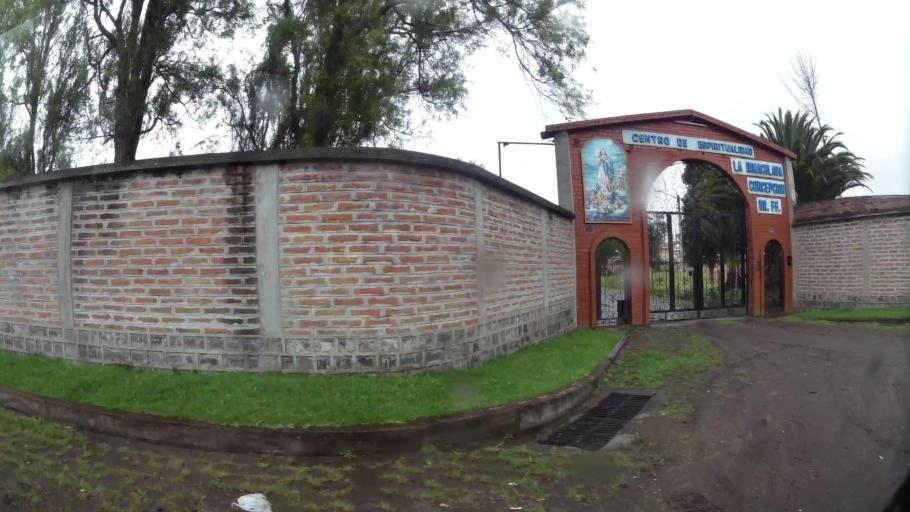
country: EC
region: Pichincha
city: Sangolqui
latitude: -0.2998
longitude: -78.4448
